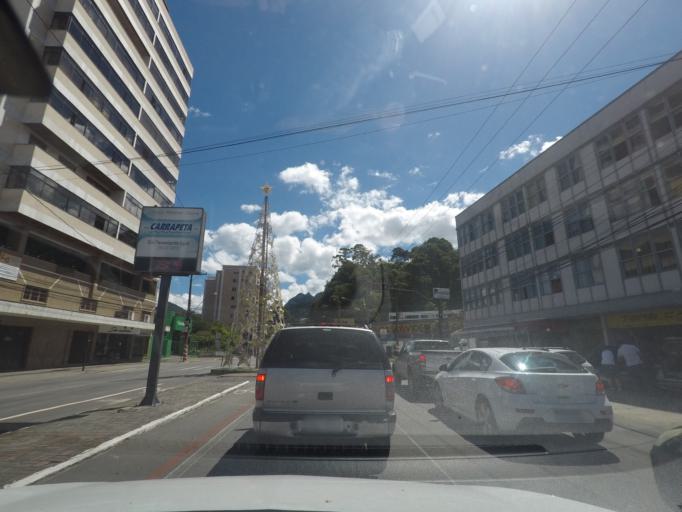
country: BR
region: Rio de Janeiro
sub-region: Teresopolis
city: Teresopolis
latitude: -22.4228
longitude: -42.9771
